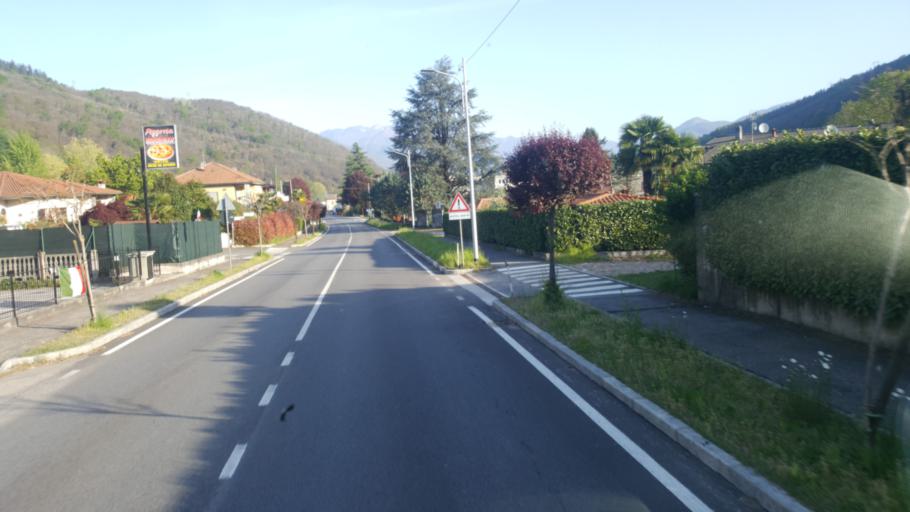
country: IT
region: Lombardy
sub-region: Provincia di Varese
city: Mesenzana
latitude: 45.9634
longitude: 8.7542
